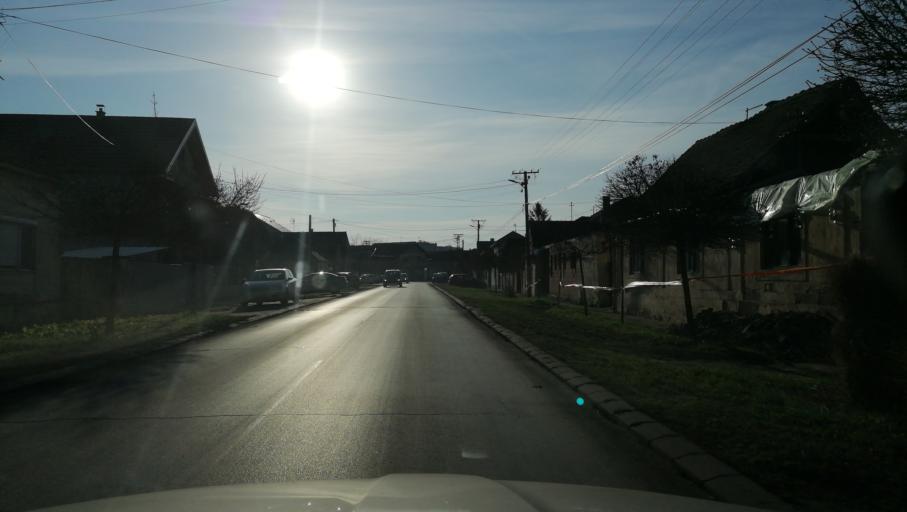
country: RS
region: Autonomna Pokrajina Vojvodina
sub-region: Sremski Okrug
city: Sremska Mitrovica
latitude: 44.9681
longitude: 19.6158
